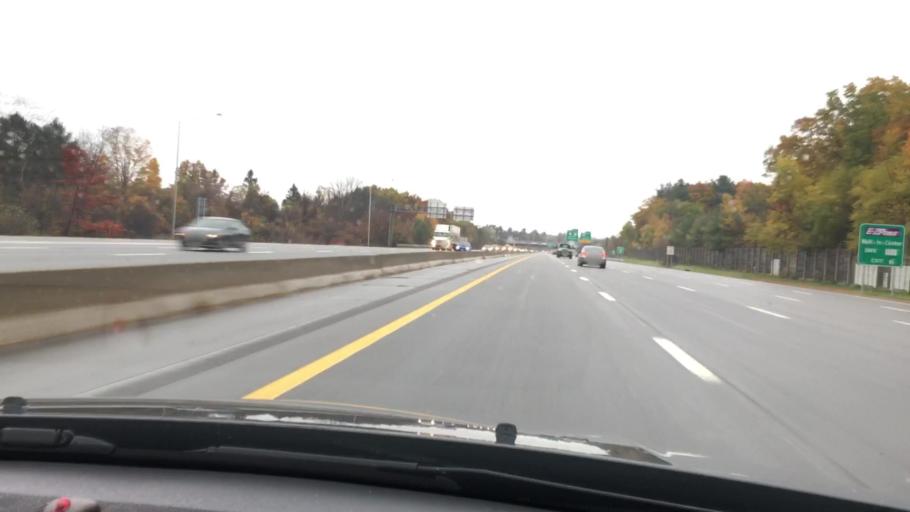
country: US
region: New Hampshire
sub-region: Hillsborough County
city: Nashua
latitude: 42.7848
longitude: -71.4948
